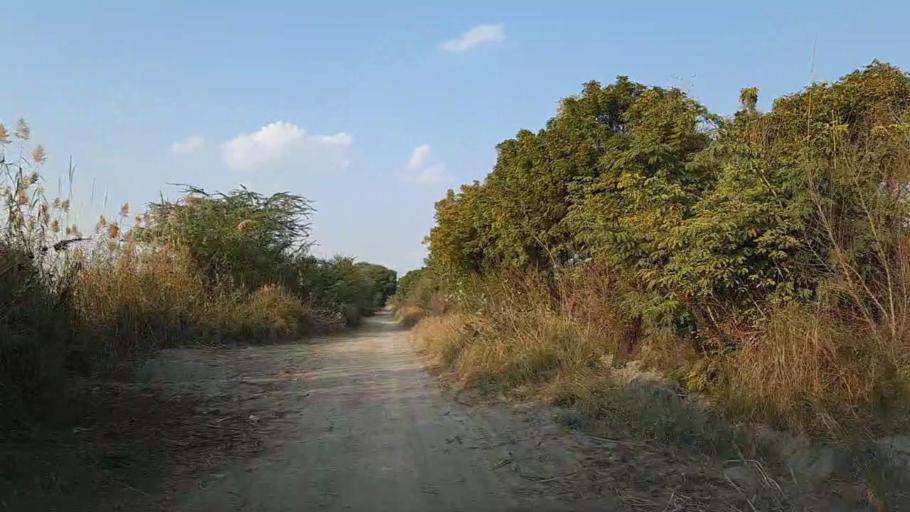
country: PK
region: Sindh
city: Jam Sahib
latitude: 26.3418
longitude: 68.5816
